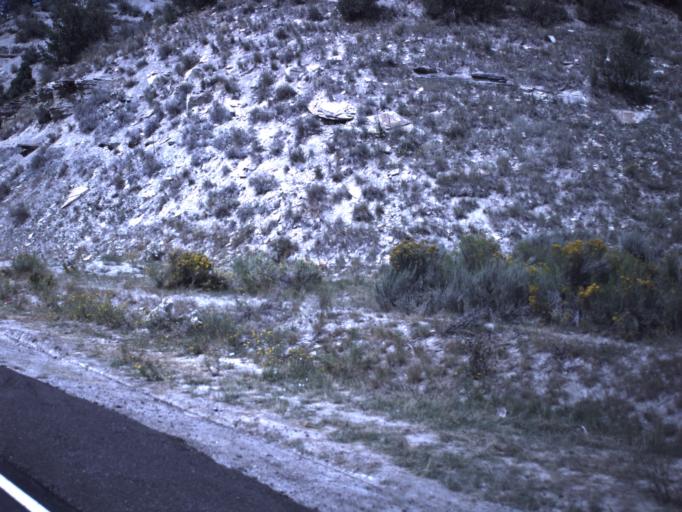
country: US
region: Utah
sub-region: Carbon County
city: Helper
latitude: 39.9288
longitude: -110.6782
